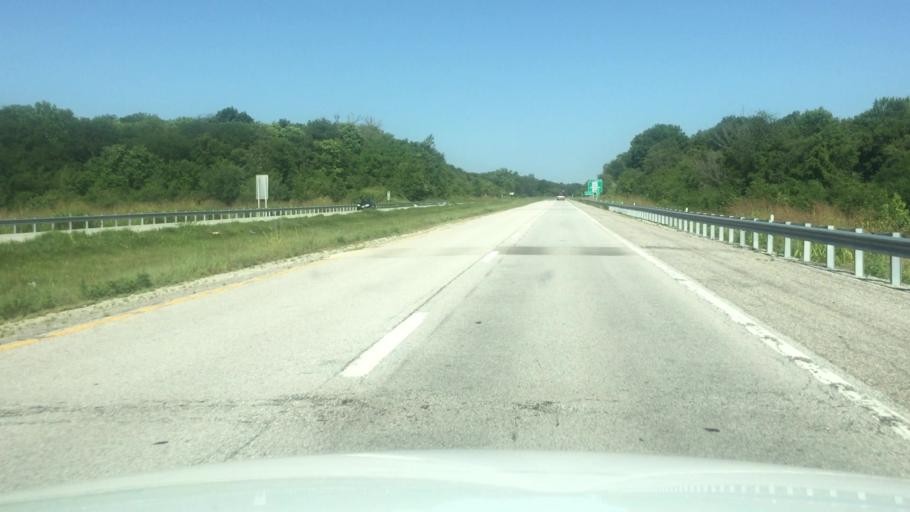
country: US
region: Missouri
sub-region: Buchanan County
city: Saint Joseph
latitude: 39.7173
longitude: -94.8220
